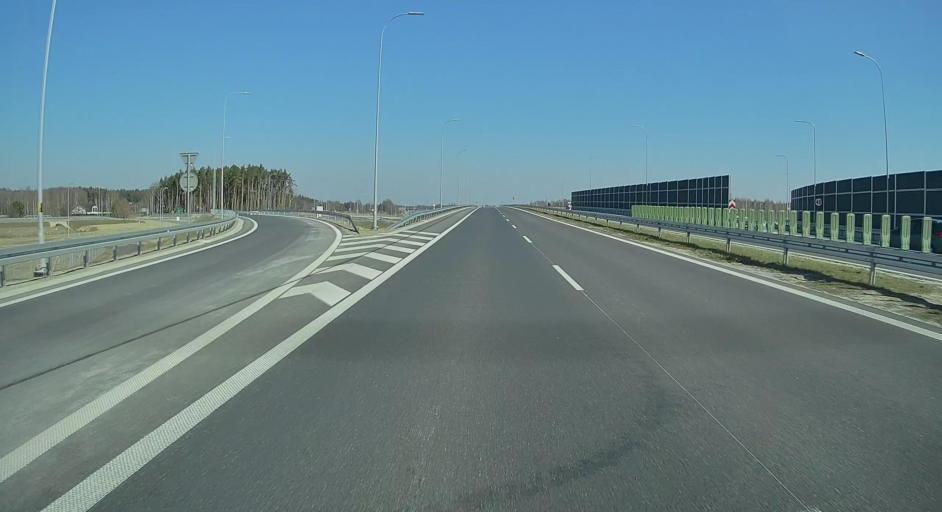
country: PL
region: Subcarpathian Voivodeship
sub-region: Powiat lezajski
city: Letownia
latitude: 50.3313
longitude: 22.1920
